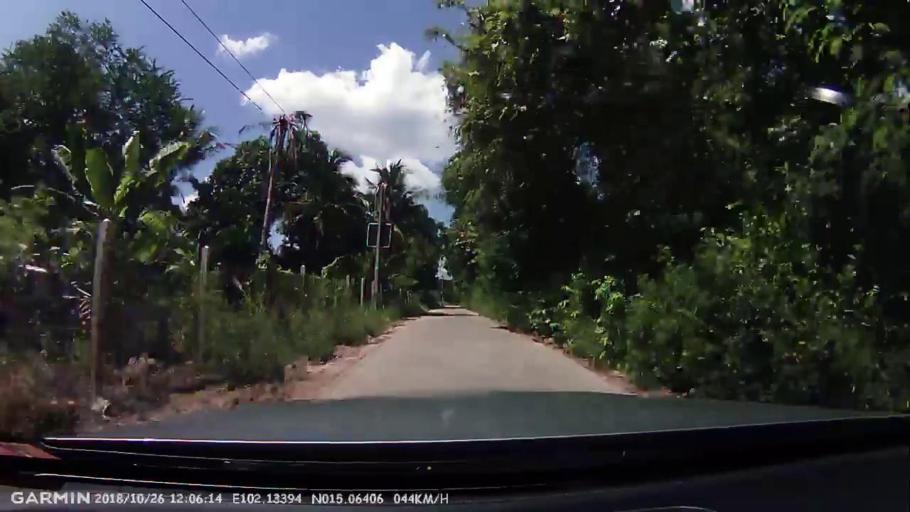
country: TH
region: Nakhon Ratchasima
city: Nakhon Ratchasima
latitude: 15.0641
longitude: 102.1338
